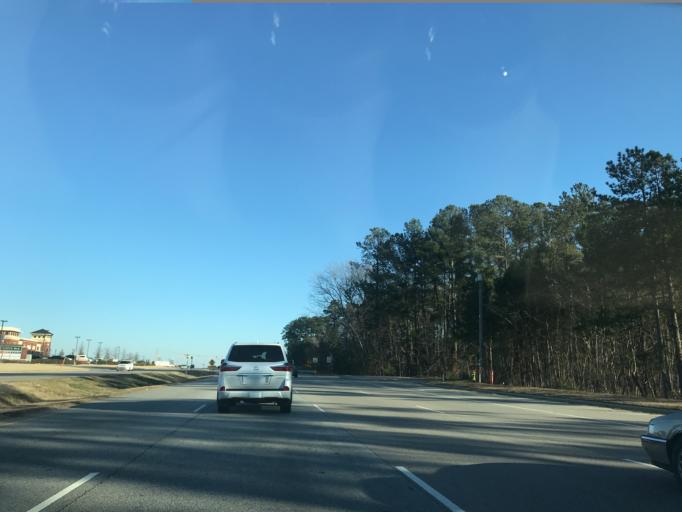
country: US
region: North Carolina
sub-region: Wake County
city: Garner
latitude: 35.6972
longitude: -78.5882
